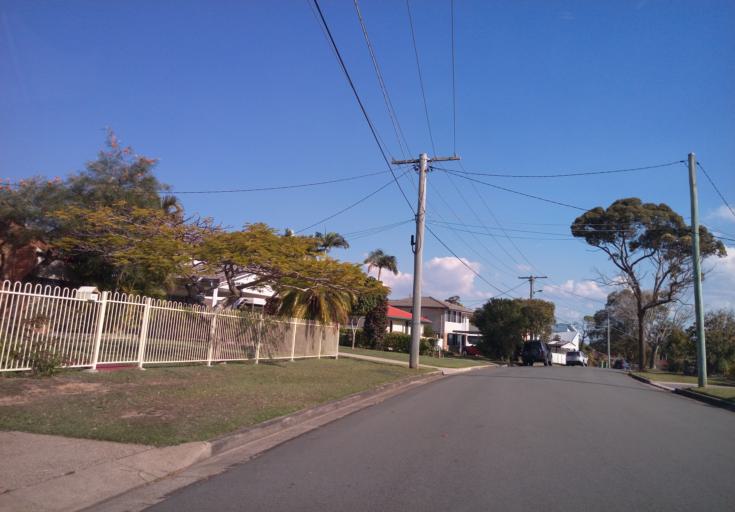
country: AU
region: Queensland
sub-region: Redland
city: Wellington Point
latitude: -27.5149
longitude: 153.2177
